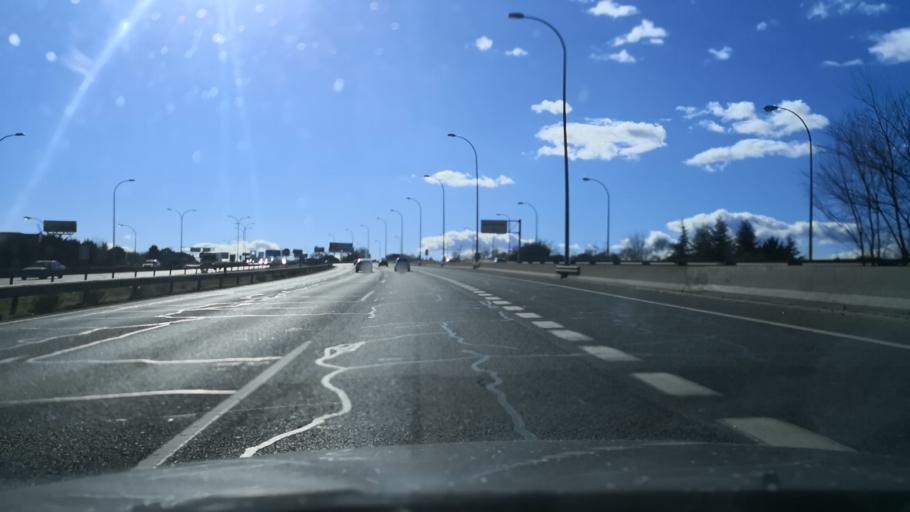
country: ES
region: Madrid
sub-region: Provincia de Madrid
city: Alcobendas
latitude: 40.5297
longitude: -3.6458
